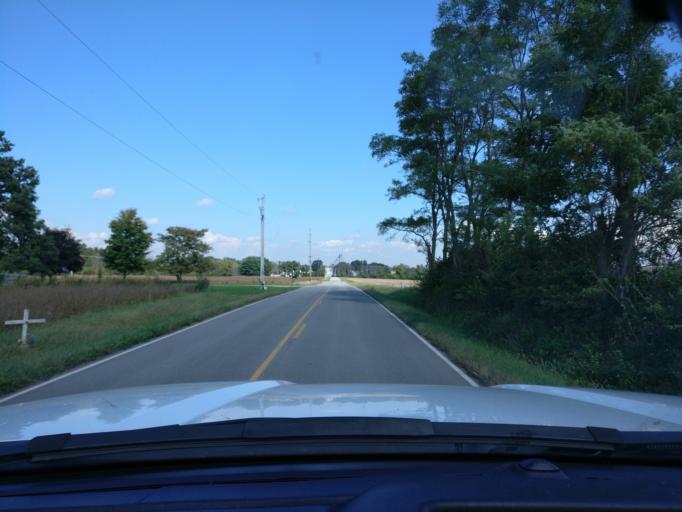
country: US
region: Ohio
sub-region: Warren County
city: Waynesville
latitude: 39.4717
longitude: -83.9947
